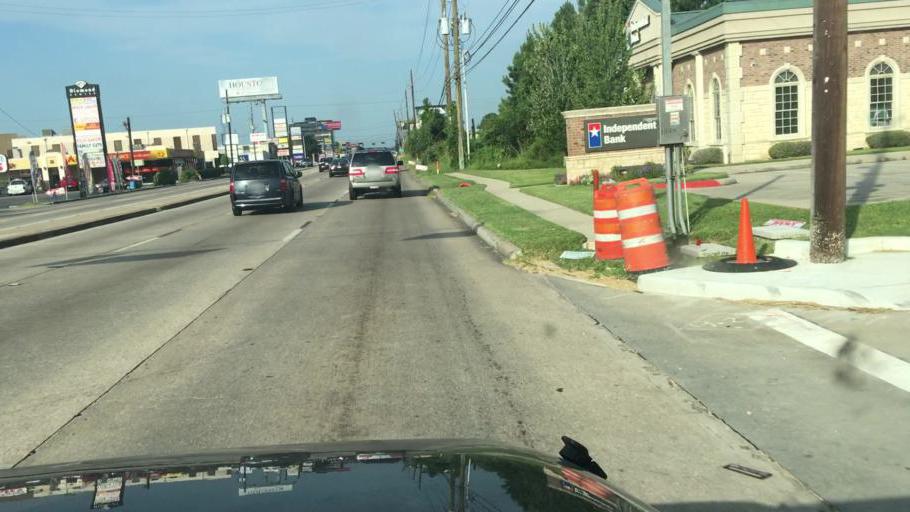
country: US
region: Texas
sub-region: Harris County
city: Spring
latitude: 30.0159
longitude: -95.4469
